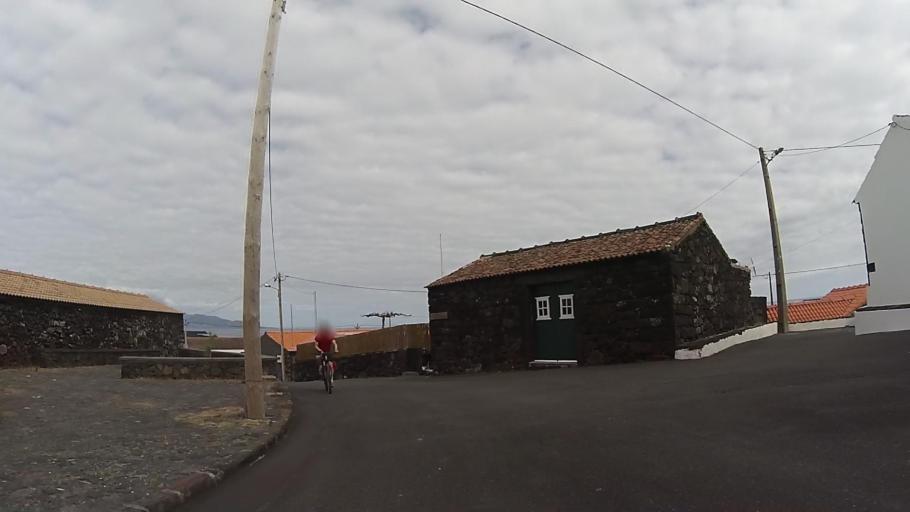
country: PT
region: Azores
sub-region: Madalena
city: Madalena
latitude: 38.5554
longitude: -28.4463
